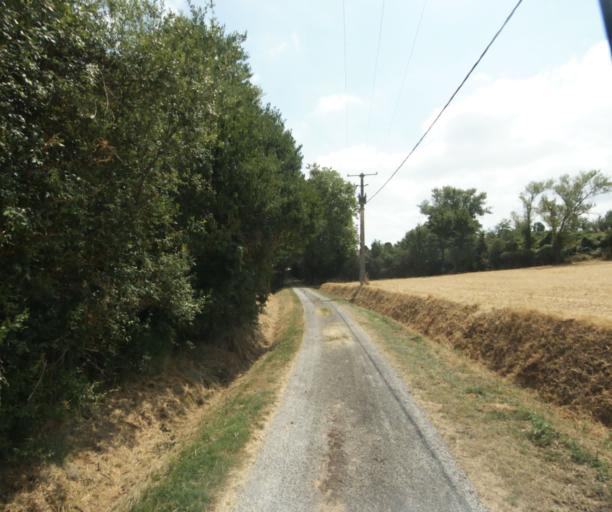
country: FR
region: Midi-Pyrenees
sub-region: Departement de la Haute-Garonne
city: Revel
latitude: 43.4360
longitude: 1.9751
